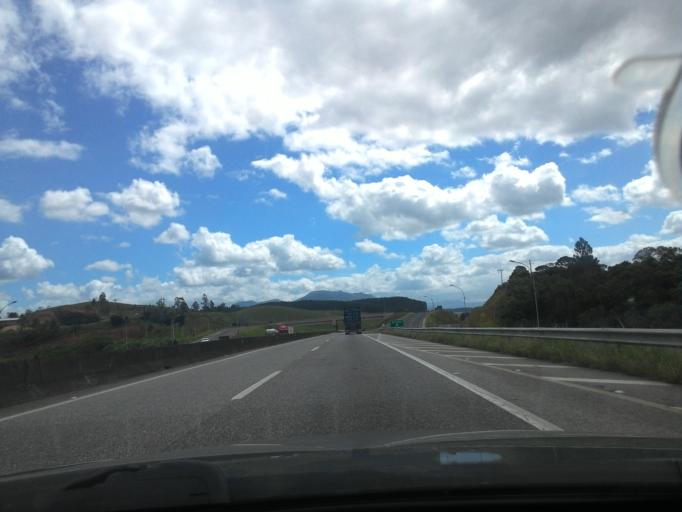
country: BR
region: Sao Paulo
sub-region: Jacupiranga
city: Jacupiranga
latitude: -24.7077
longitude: -48.0163
